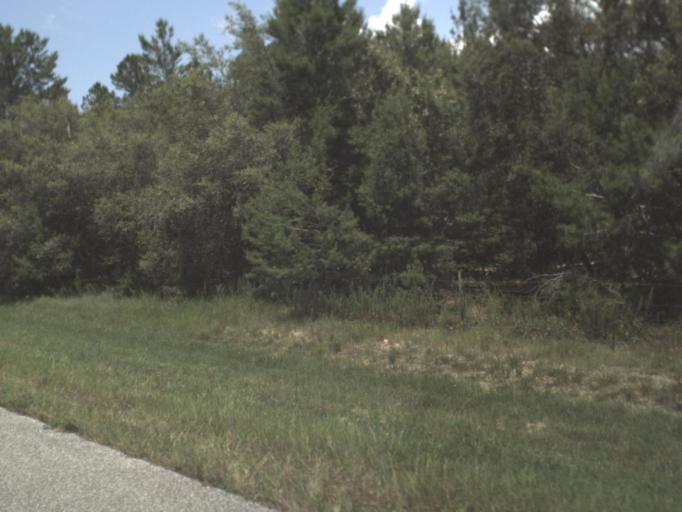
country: US
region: Florida
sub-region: Citrus County
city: Sugarmill Woods
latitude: 28.6972
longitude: -82.5101
